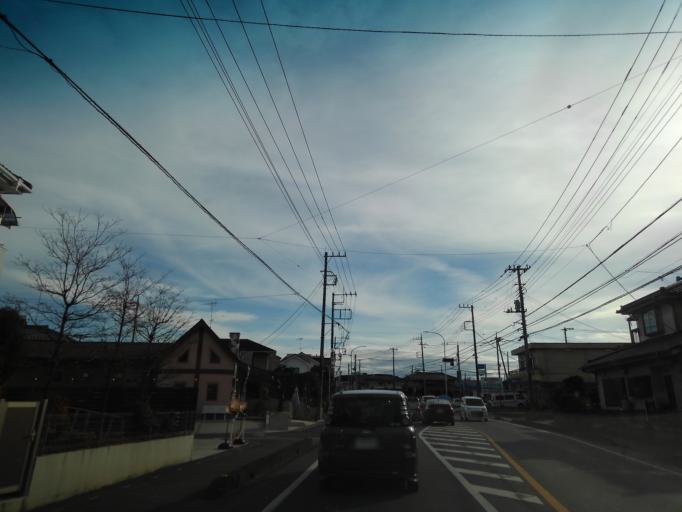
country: JP
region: Saitama
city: Morohongo
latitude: 35.8995
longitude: 139.3349
